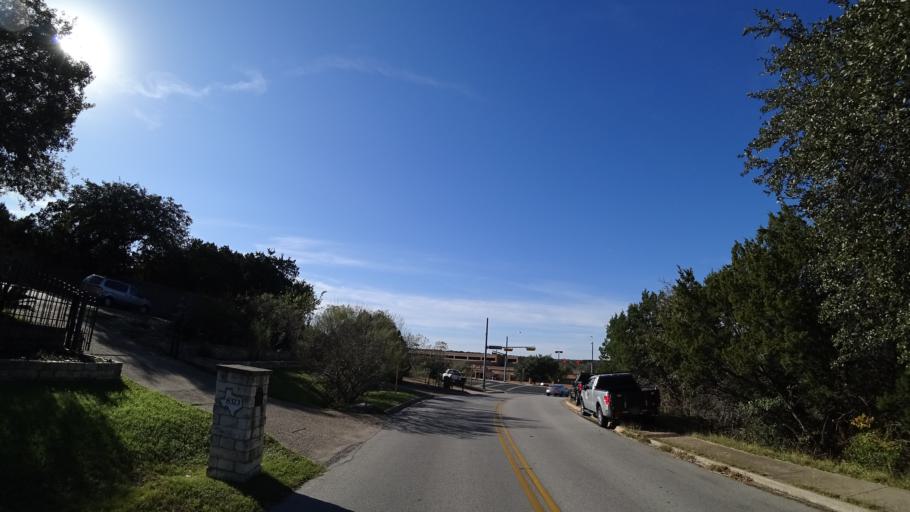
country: US
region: Texas
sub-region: Williamson County
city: Jollyville
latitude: 30.4280
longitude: -97.7825
